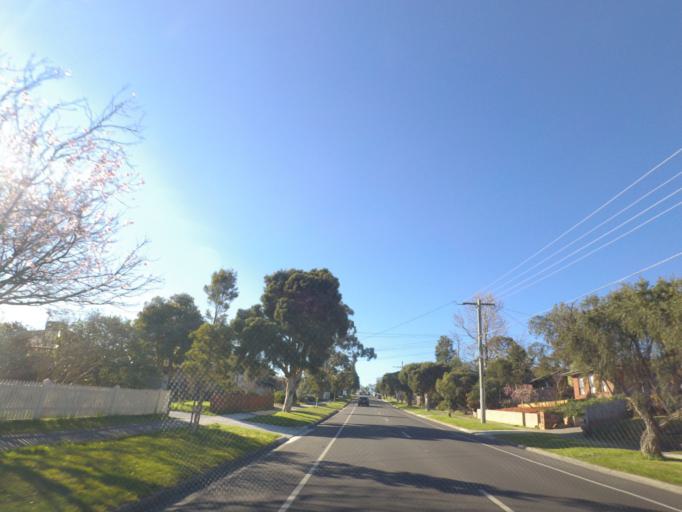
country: AU
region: Victoria
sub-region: Yarra Ranges
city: Kilsyth
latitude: -37.7943
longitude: 145.3138
